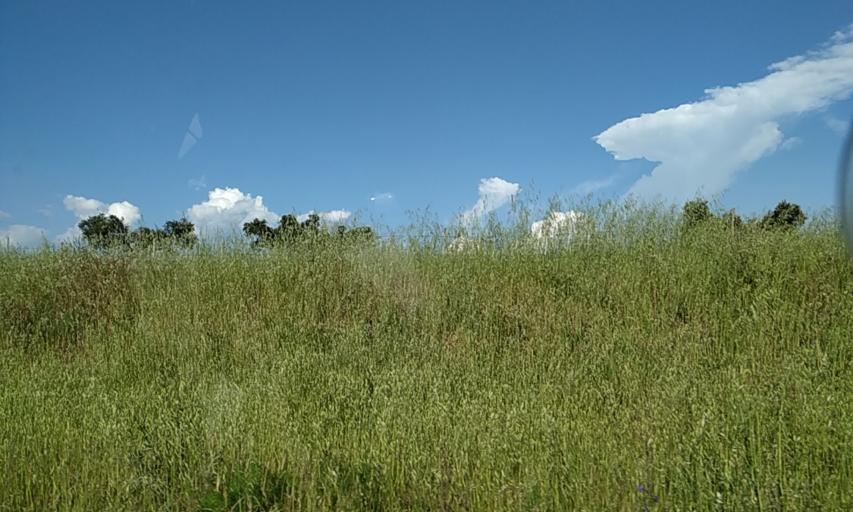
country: PT
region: Portalegre
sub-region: Portalegre
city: Urra
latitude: 39.0941
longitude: -7.4372
